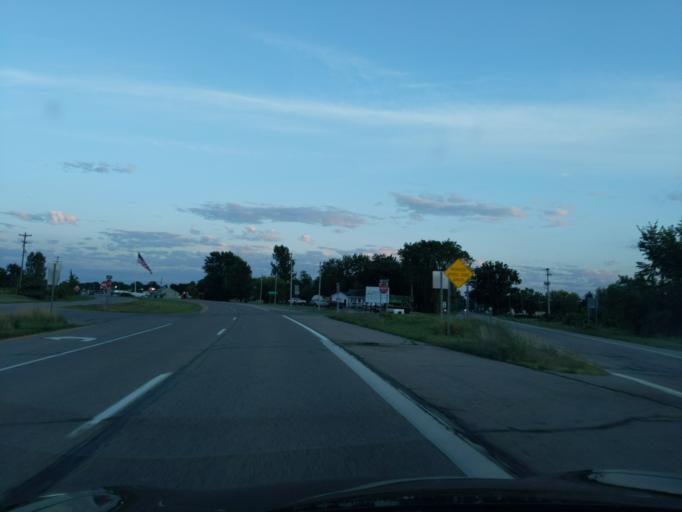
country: US
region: Michigan
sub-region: Clinton County
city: Saint Johns
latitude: 43.0185
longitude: -84.5628
